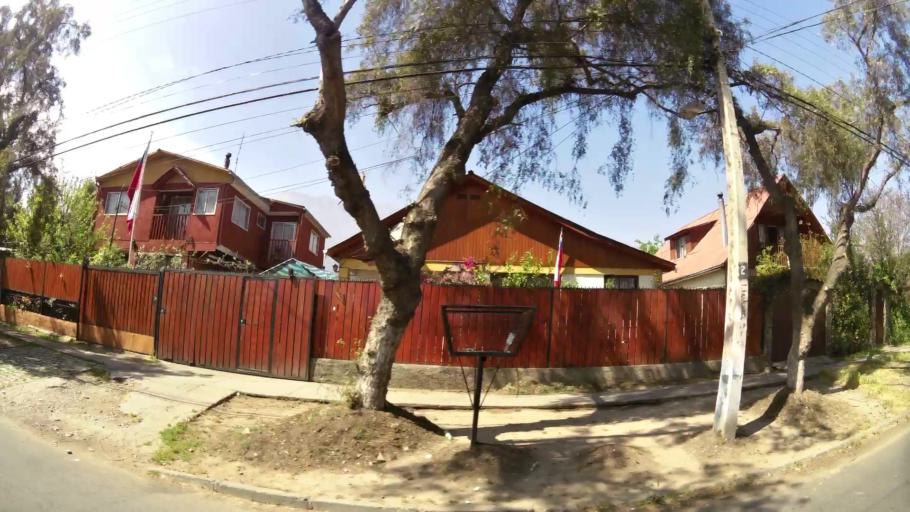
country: CL
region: Santiago Metropolitan
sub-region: Provincia de Santiago
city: Villa Presidente Frei, Nunoa, Santiago, Chile
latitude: -33.4647
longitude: -70.5360
